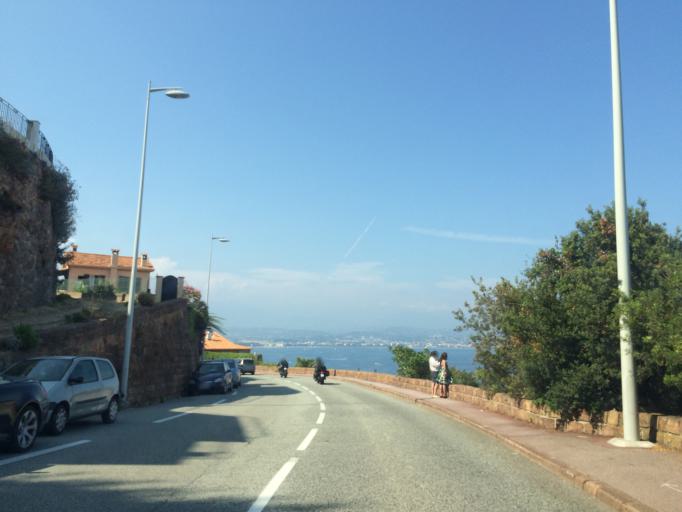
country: FR
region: Provence-Alpes-Cote d'Azur
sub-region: Departement des Alpes-Maritimes
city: Theoule-sur-Mer
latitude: 43.5036
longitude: 6.9534
